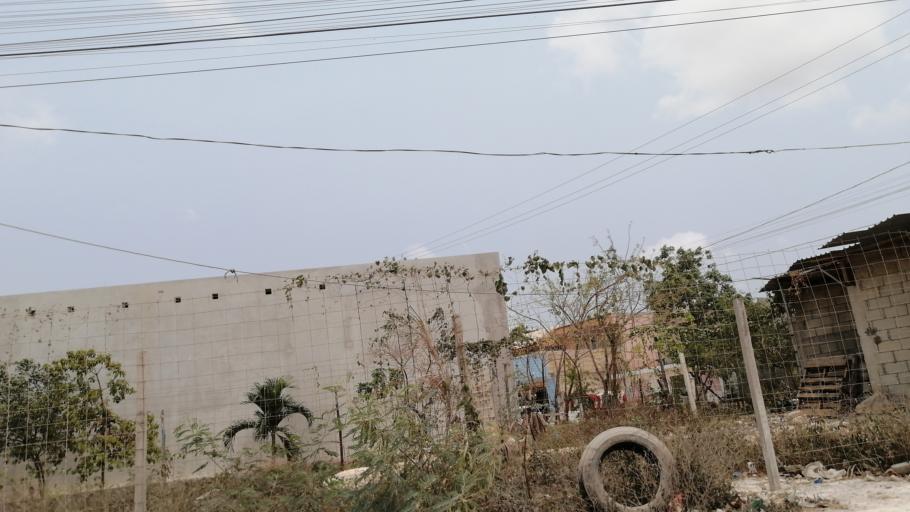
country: MX
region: Quintana Roo
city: Cancun
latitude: 21.1355
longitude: -86.8979
